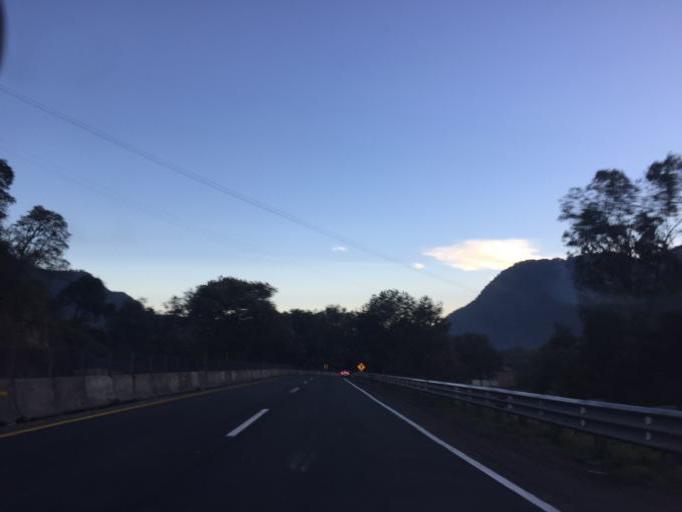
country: MX
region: Veracruz
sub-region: Huiloapan de Cuauhtemoc
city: Huiloapan de Cuauhtemoc
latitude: 18.8185
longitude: -97.1660
